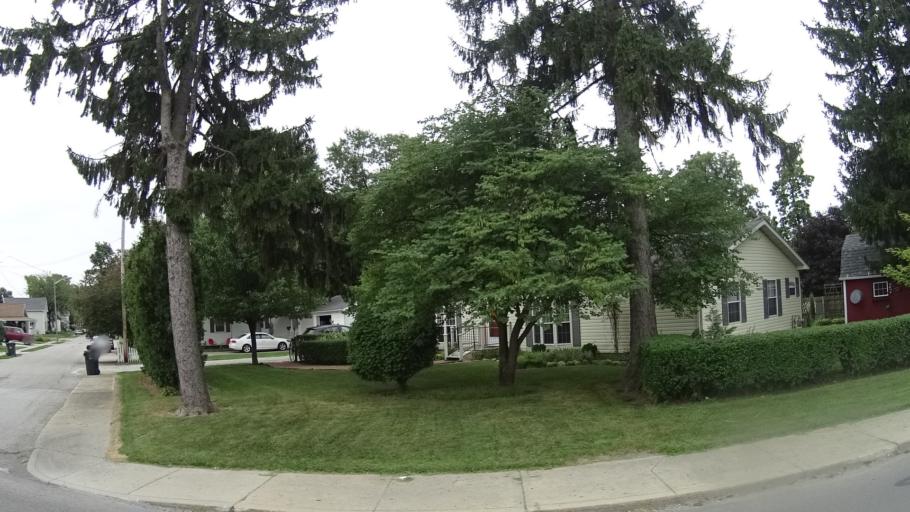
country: US
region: Indiana
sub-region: Madison County
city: Lapel
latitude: 40.0668
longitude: -85.8492
